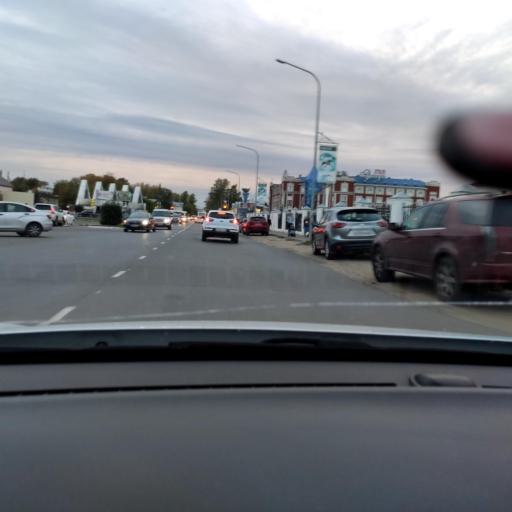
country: RU
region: Mariy-El
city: Volzhsk
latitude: 55.8617
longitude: 48.3737
